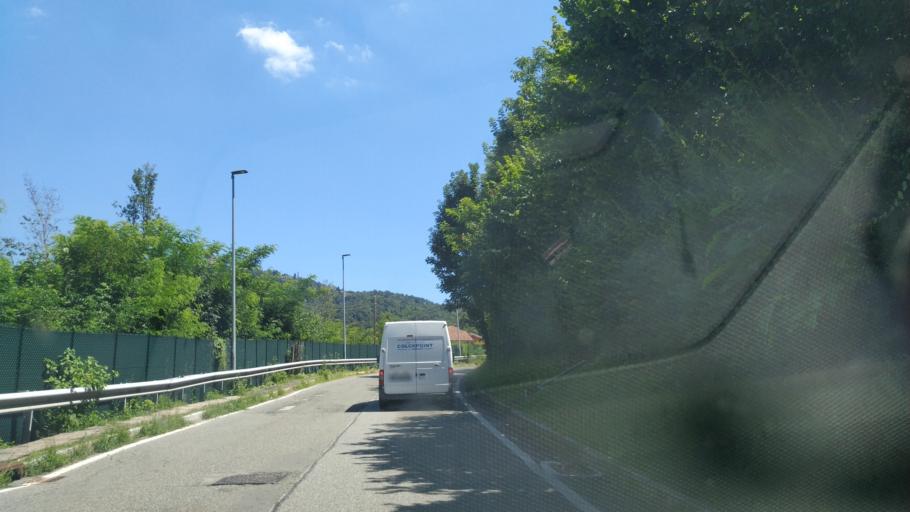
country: IT
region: Piedmont
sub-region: Provincia di Torino
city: San Mauro Torinese
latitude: 45.0834
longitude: 7.7434
